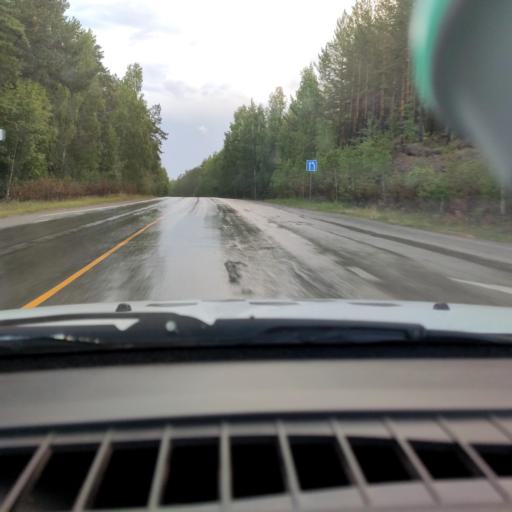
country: RU
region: Chelyabinsk
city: Kyshtym
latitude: 55.7349
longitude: 60.5360
